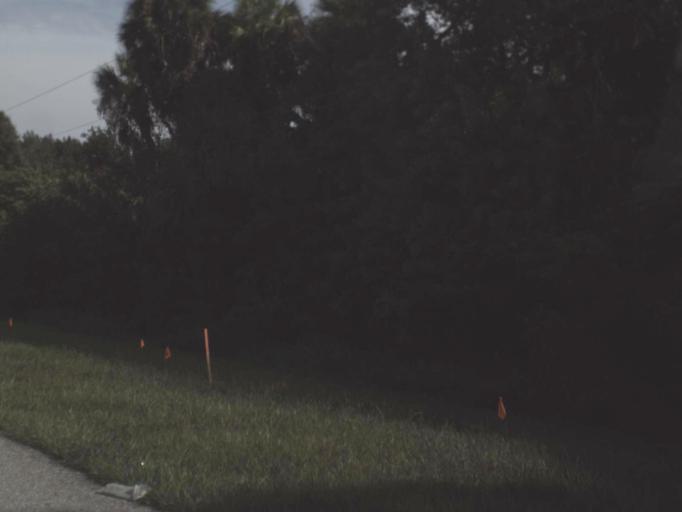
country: US
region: Florida
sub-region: Lee County
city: Fort Myers Shores
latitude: 26.7037
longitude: -81.7602
